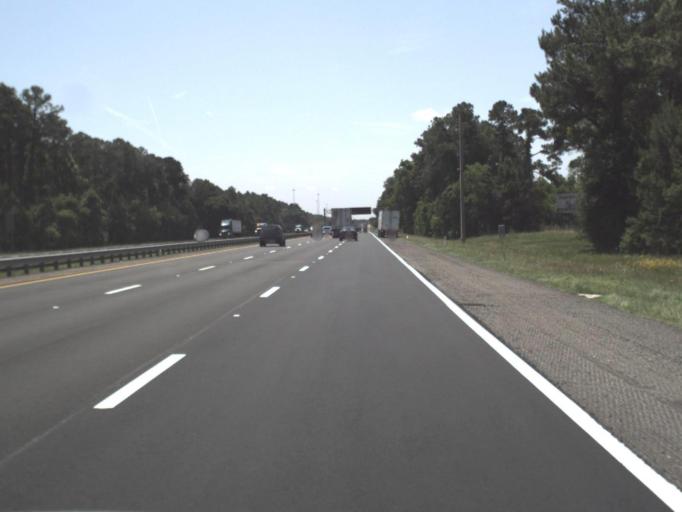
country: US
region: Florida
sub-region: Nassau County
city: Yulee
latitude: 30.5288
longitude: -81.6365
